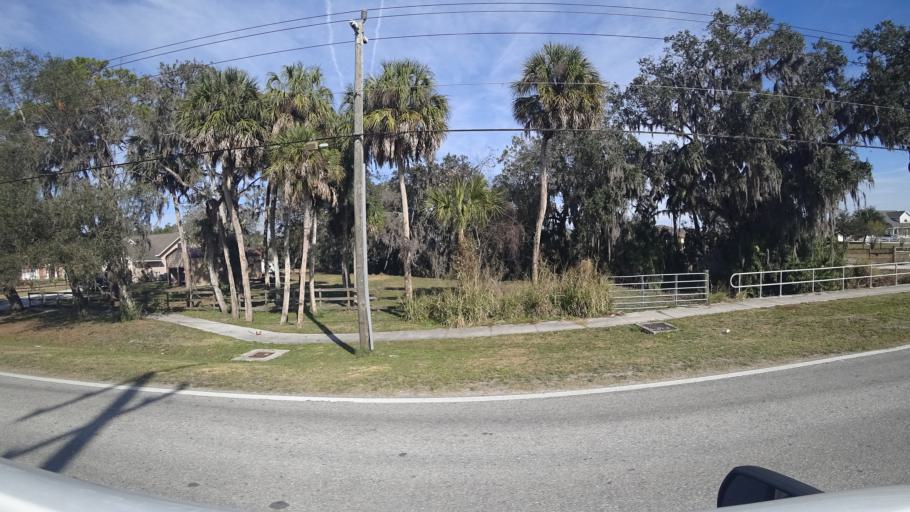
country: US
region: Florida
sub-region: Manatee County
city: Ellenton
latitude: 27.5739
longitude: -82.4935
